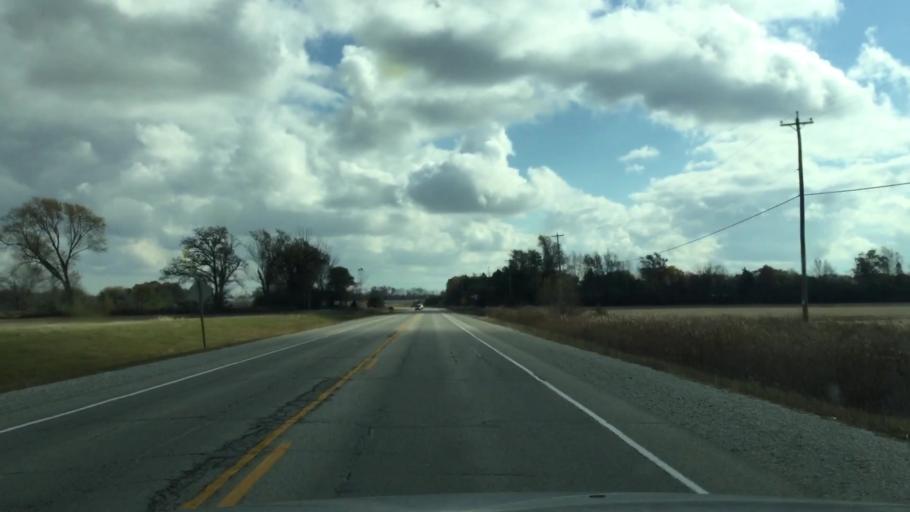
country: US
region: Wisconsin
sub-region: Racine County
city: Eagle Lake
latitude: 42.7410
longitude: -88.1036
